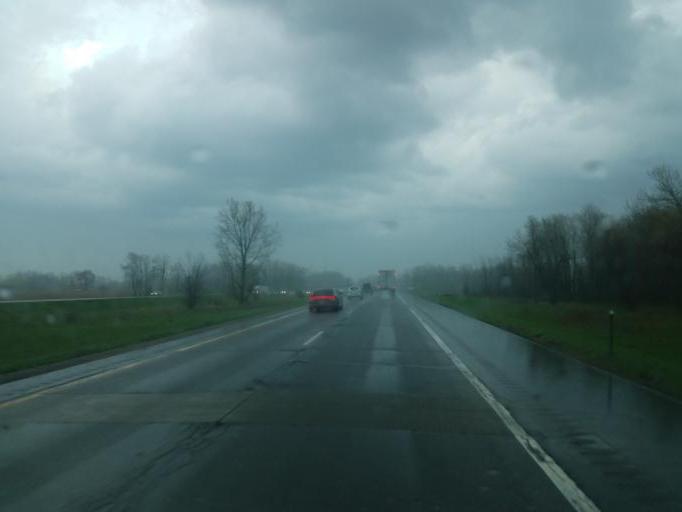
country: US
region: Michigan
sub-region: Ingham County
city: Webberville
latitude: 42.6509
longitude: -84.1542
